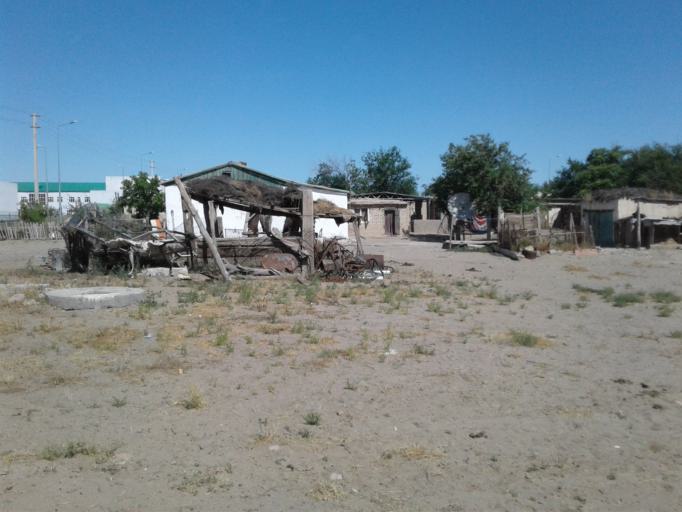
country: TM
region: Mary
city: Bayramaly
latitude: 38.0879
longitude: 62.7990
